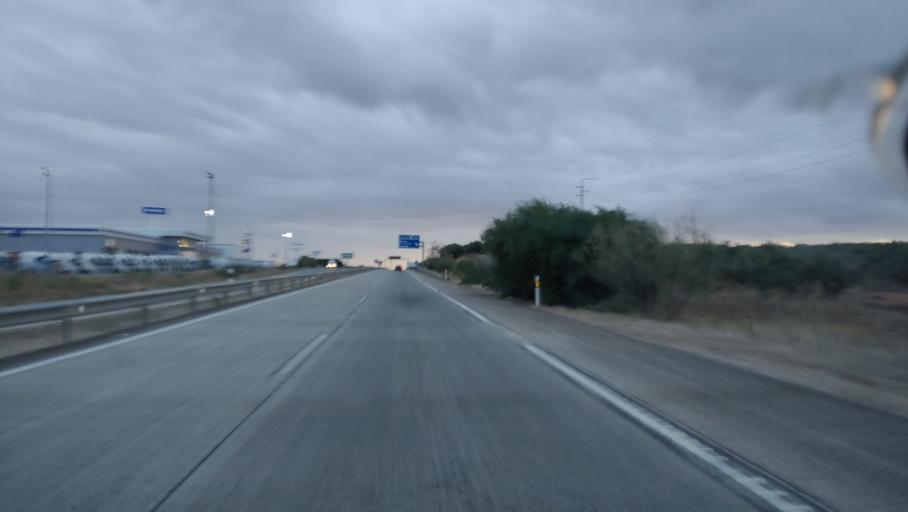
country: ES
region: Andalusia
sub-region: Provincia de Jaen
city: Guarroman
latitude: 38.1491
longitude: -3.7220
